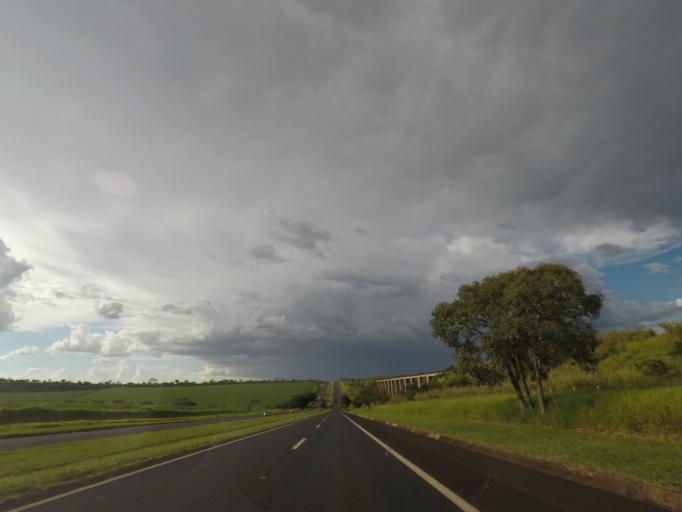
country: BR
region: Sao Paulo
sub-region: Jardinopolis
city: Jardinopolis
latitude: -21.0122
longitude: -47.8443
